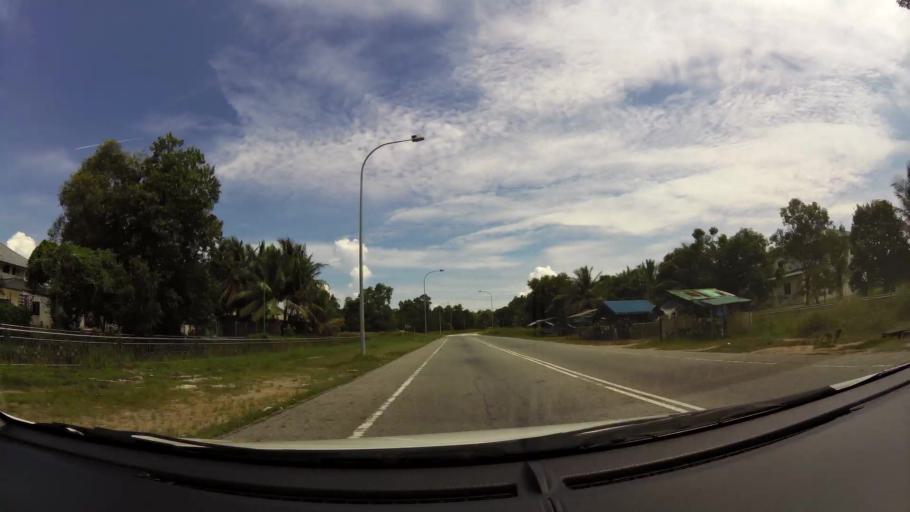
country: BN
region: Brunei and Muara
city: Bandar Seri Begawan
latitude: 4.9566
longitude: 114.9042
